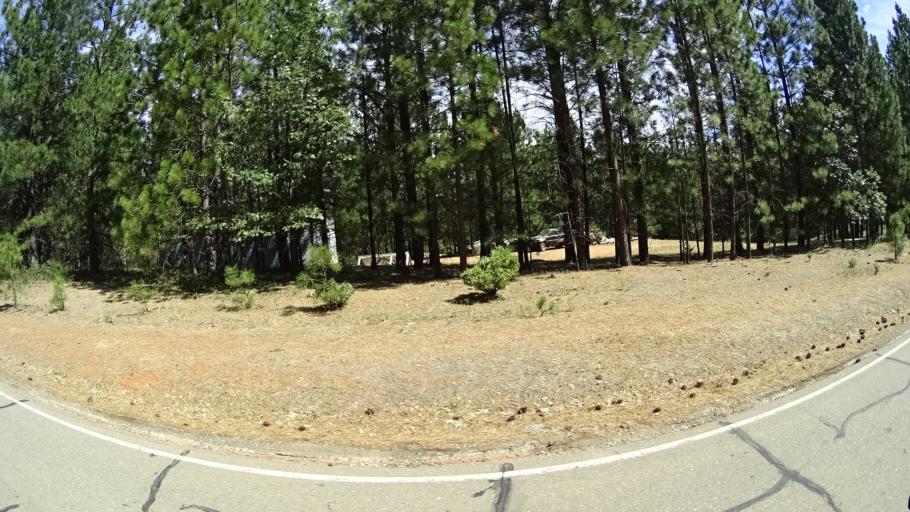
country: US
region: California
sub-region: Amador County
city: Pioneer
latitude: 38.3359
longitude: -120.5405
